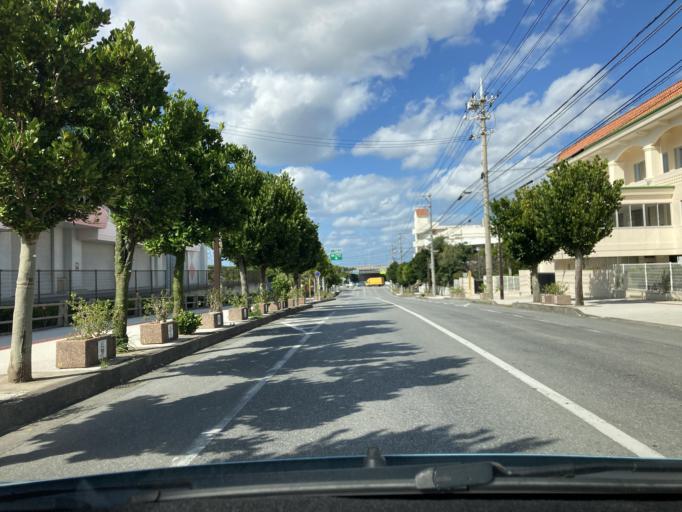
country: JP
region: Okinawa
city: Okinawa
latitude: 26.3339
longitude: 127.7904
